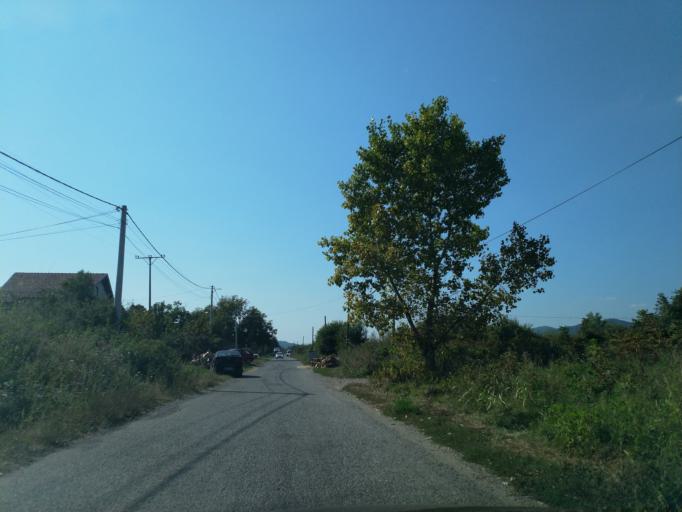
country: RS
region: Central Serbia
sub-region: Rasinski Okrug
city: Trstenik
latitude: 43.6119
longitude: 21.0272
